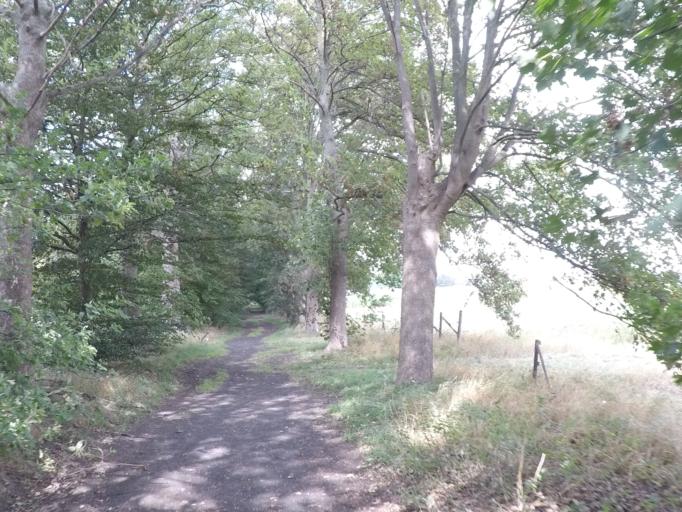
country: BE
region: Flanders
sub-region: Provincie Antwerpen
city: Ranst
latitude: 51.1858
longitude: 4.5993
